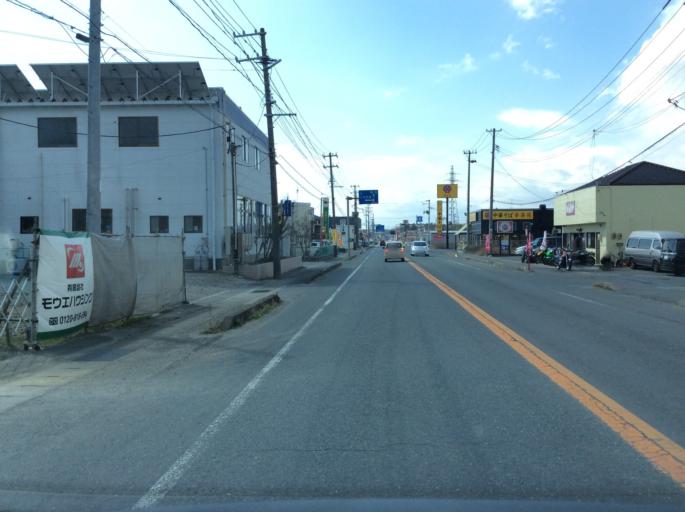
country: JP
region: Fukushima
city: Iwaki
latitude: 36.9518
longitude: 140.8639
